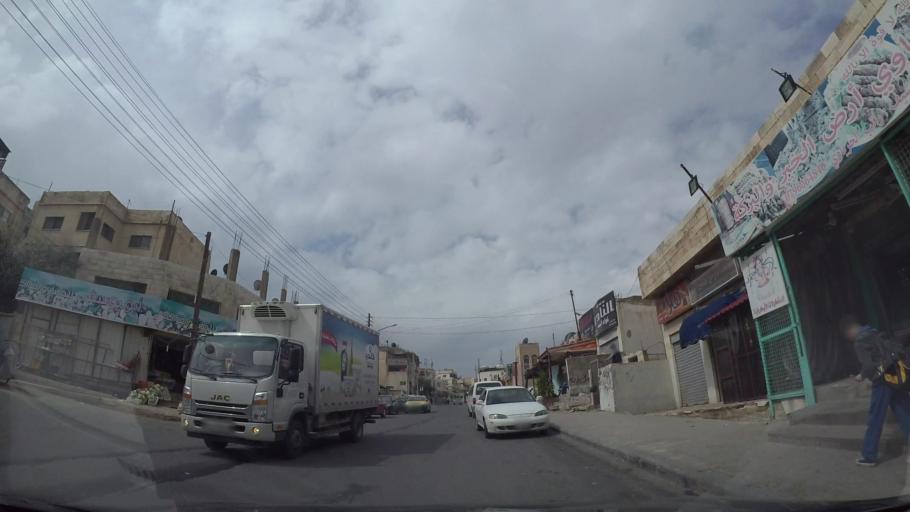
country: JO
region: Amman
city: Amman
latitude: 31.9618
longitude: 35.9542
